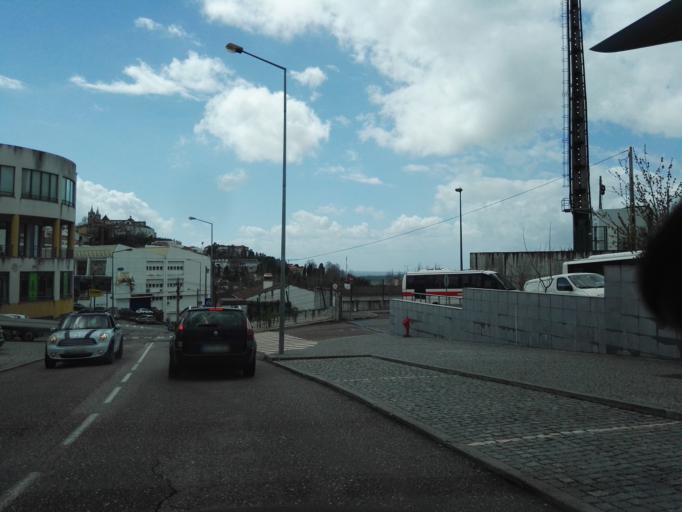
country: PT
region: Portalegre
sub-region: Portalegre
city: Portalegre
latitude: 39.2973
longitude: -7.4325
